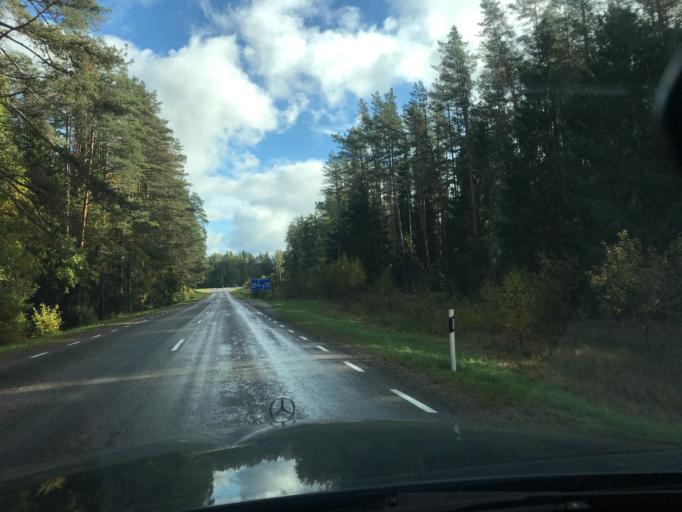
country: EE
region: Valgamaa
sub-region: Torva linn
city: Torva
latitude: 58.0094
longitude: 26.1552
